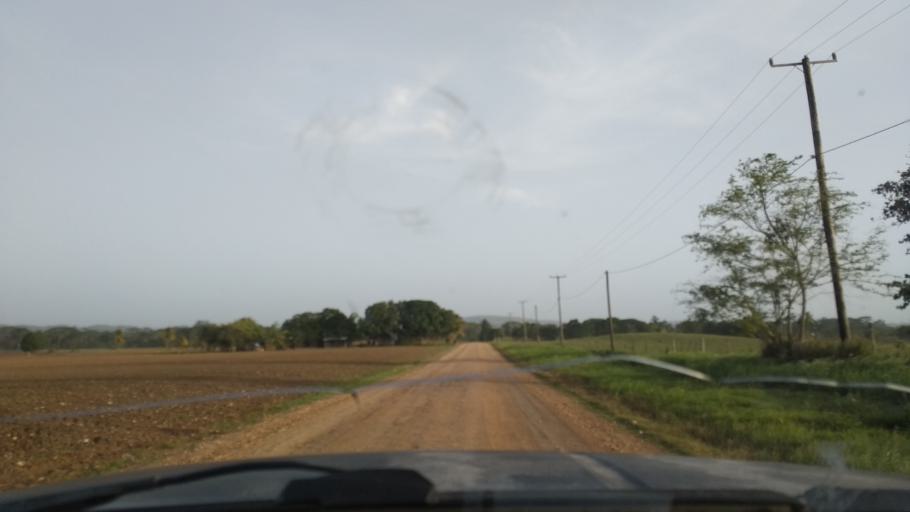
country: BZ
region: Cayo
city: San Ignacio
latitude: 17.2129
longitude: -89.0137
